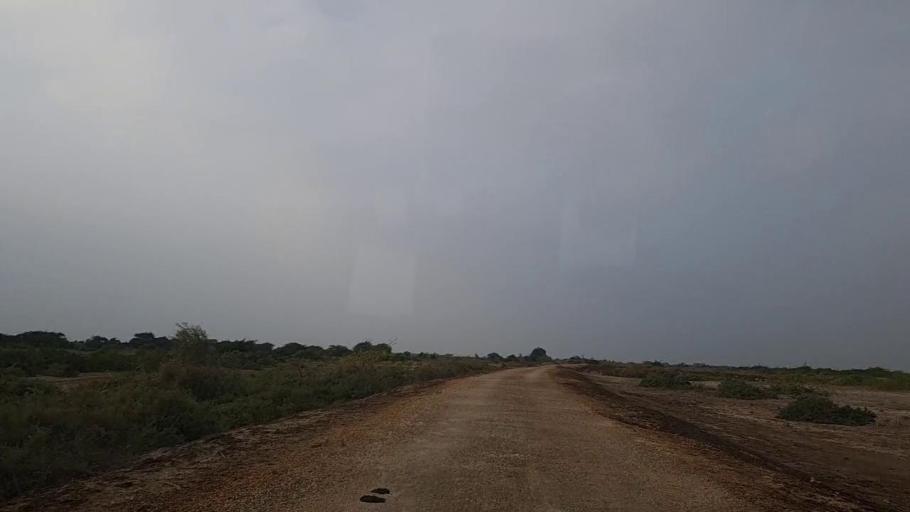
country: PK
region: Sindh
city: Mirpur Sakro
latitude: 24.6060
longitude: 67.5163
